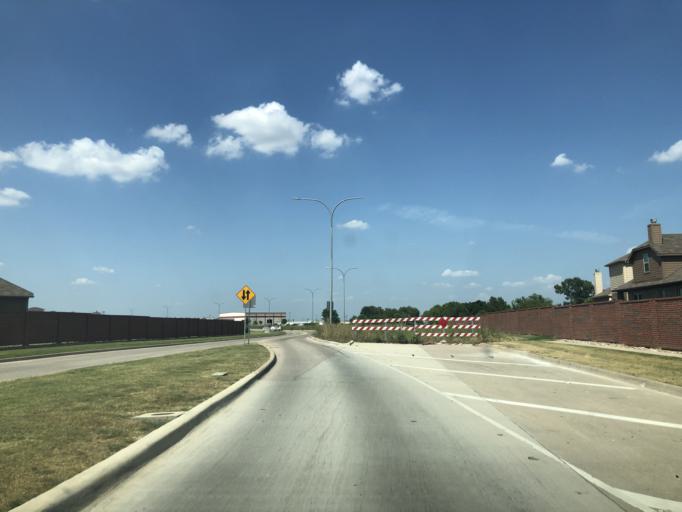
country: US
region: Texas
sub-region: Tarrant County
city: Haslet
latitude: 32.9275
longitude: -97.3246
